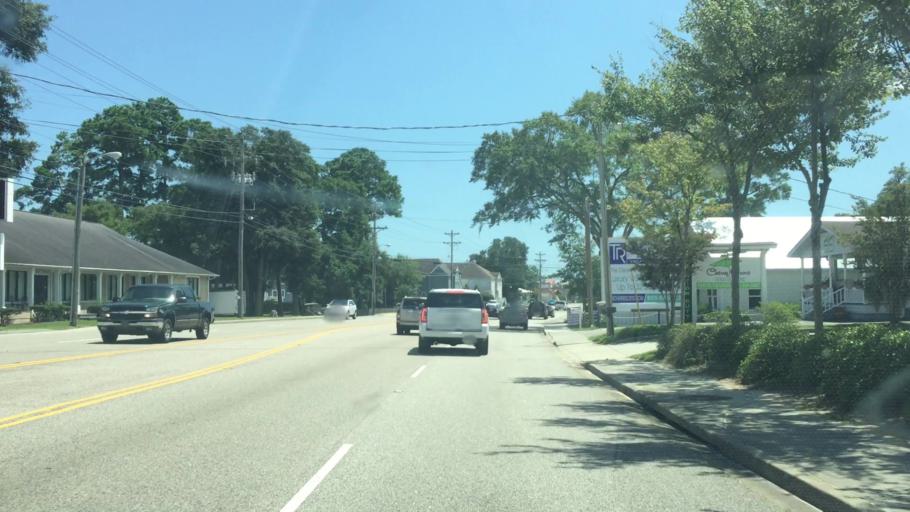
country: US
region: South Carolina
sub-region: Horry County
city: North Myrtle Beach
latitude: 33.8390
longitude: -78.6451
